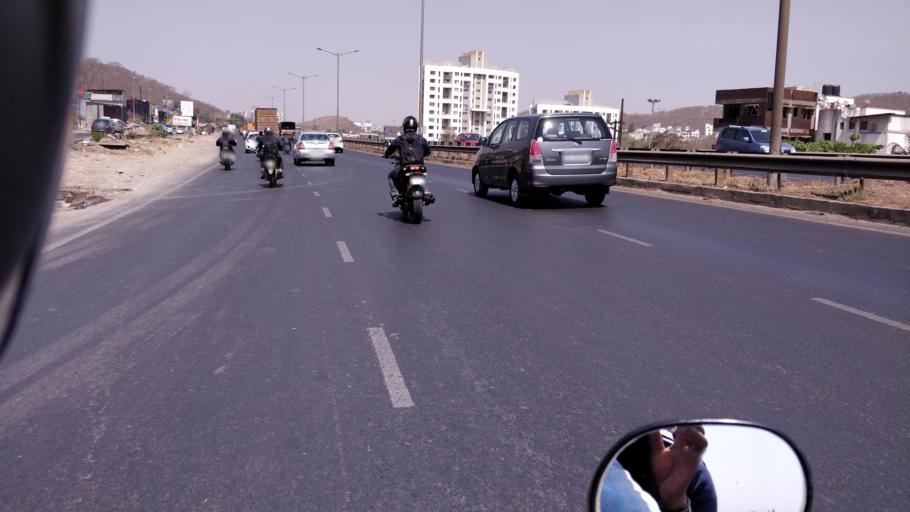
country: IN
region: Maharashtra
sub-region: Pune Division
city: Shivaji Nagar
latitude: 18.5402
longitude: 73.7800
